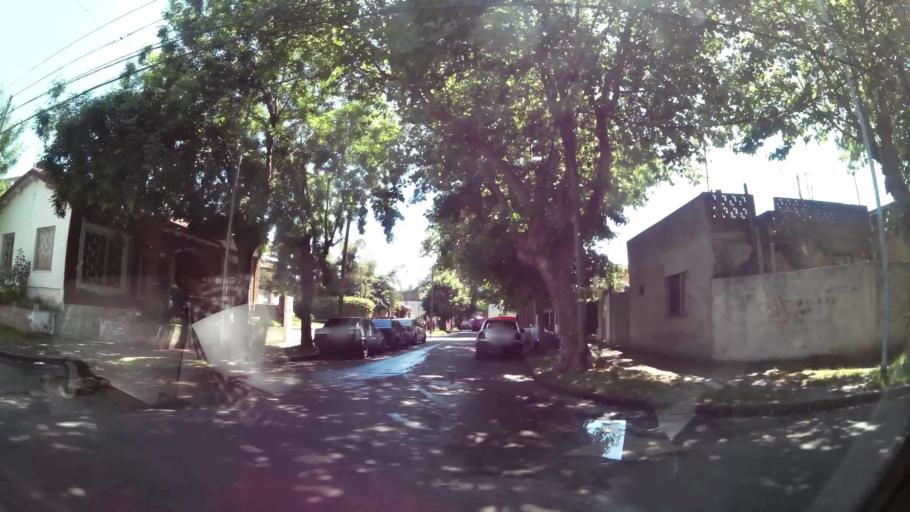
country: AR
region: Buenos Aires
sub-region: Partido de Tigre
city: Tigre
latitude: -34.4291
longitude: -58.5685
